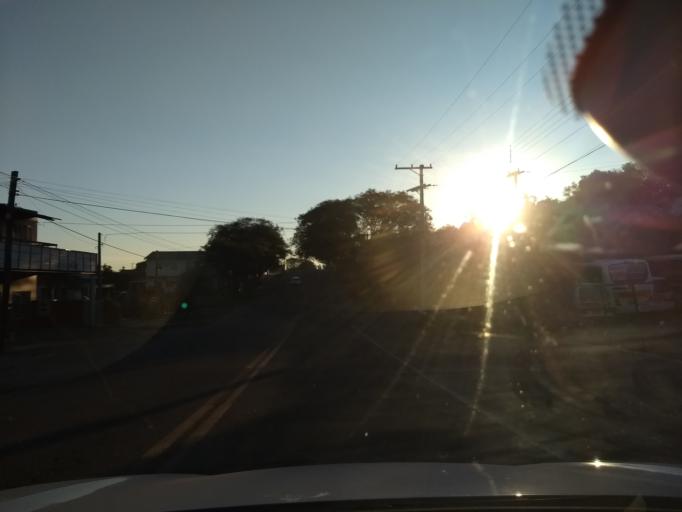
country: BR
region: Rio Grande do Sul
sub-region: Santa Cruz Do Sul
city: Santa Cruz do Sul
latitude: -29.7153
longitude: -52.5112
